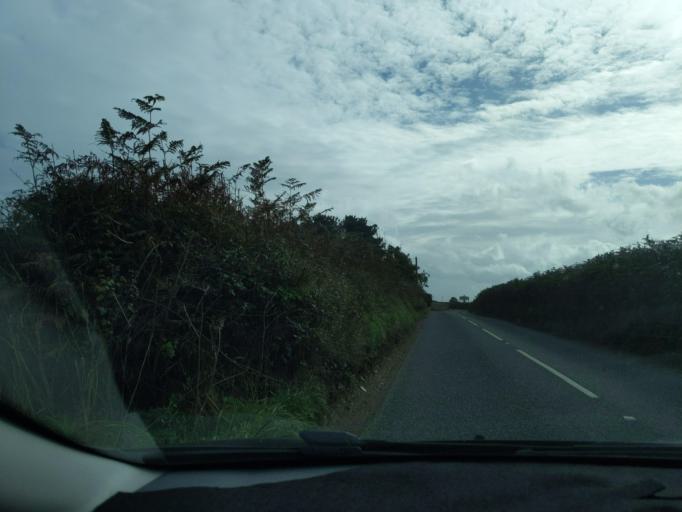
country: GB
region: England
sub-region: Cornwall
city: Mevagissey
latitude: 50.2678
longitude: -4.8298
